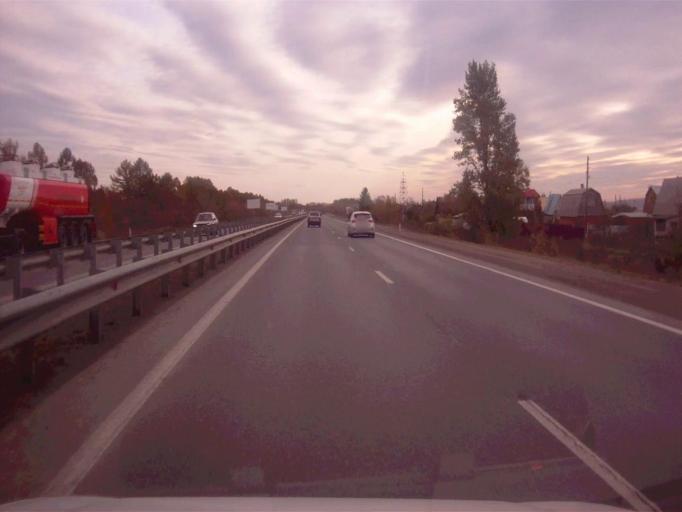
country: RU
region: Chelyabinsk
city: Novosineglazovskiy
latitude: 55.0262
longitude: 61.4502
